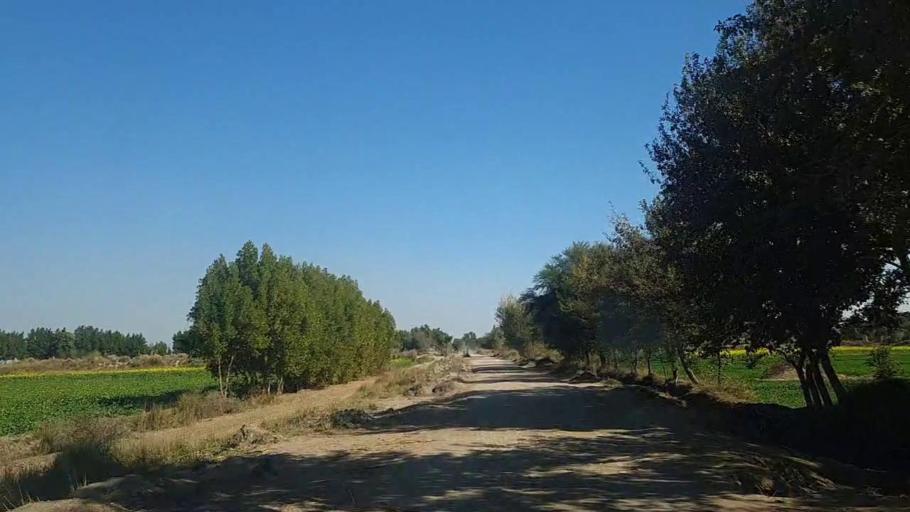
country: PK
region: Sindh
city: Sanghar
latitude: 26.2091
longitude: 68.9077
